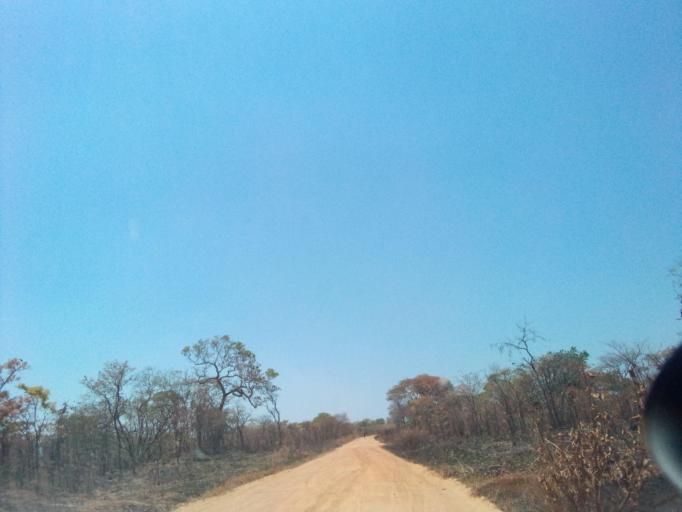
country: ZM
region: Northern
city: Mpika
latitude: -12.2540
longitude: 30.6815
